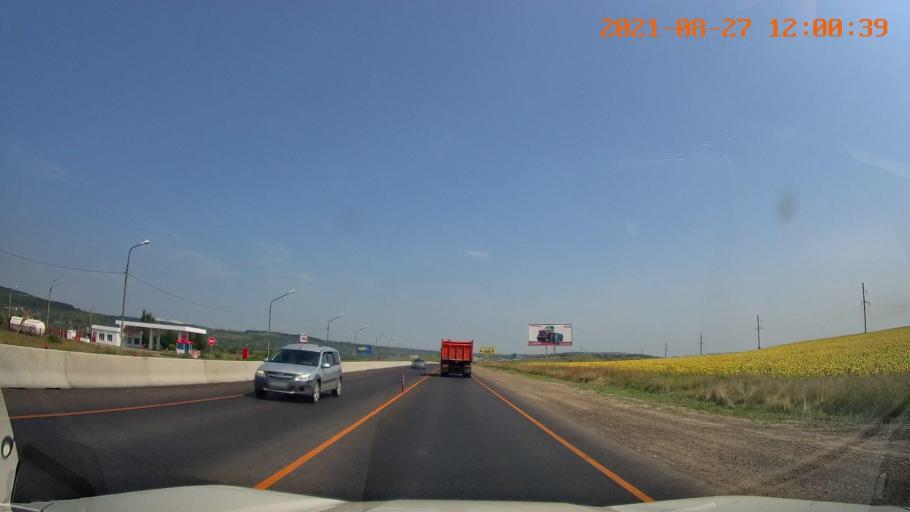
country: RU
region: Stavropol'skiy
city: Tatarka
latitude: 44.9471
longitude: 41.9274
